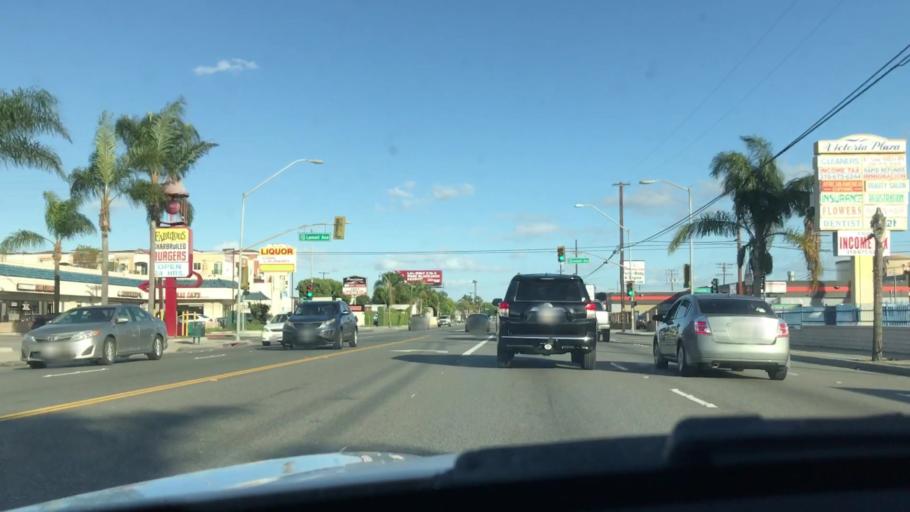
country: US
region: California
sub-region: Los Angeles County
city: Alondra Park
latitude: 33.9019
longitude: -118.3315
